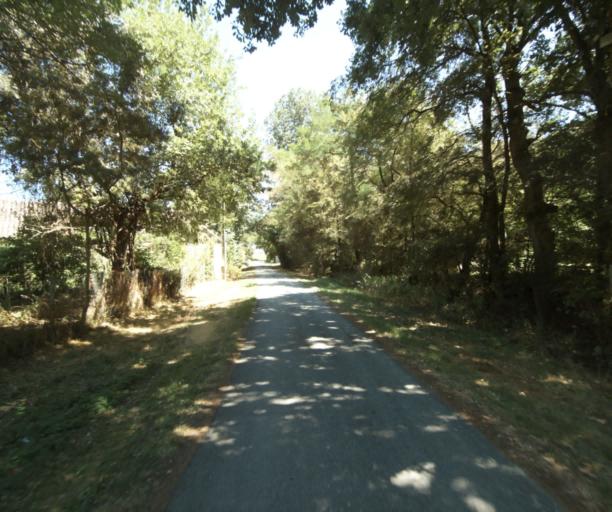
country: FR
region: Midi-Pyrenees
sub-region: Departement de la Haute-Garonne
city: Saint-Felix-Lauragais
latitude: 43.4599
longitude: 1.9428
